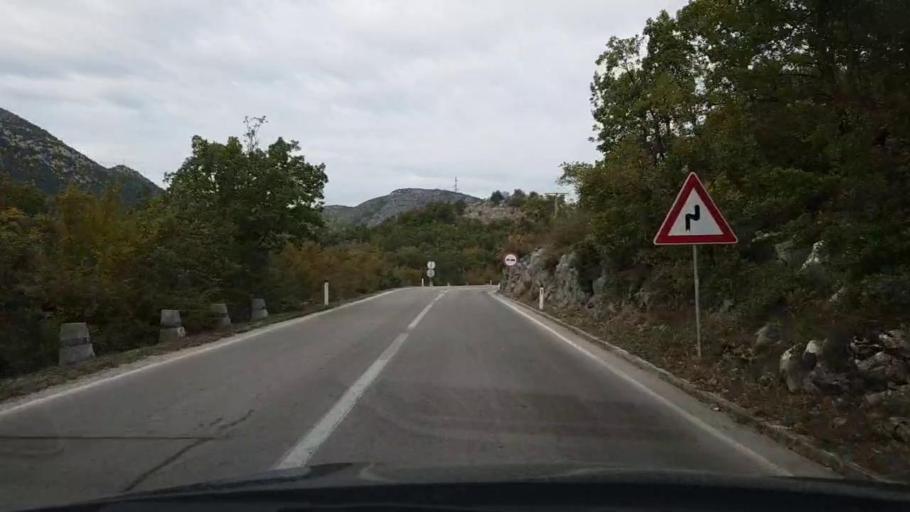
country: HR
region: Dubrovacko-Neretvanska
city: Cibaca
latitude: 42.6606
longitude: 18.2107
